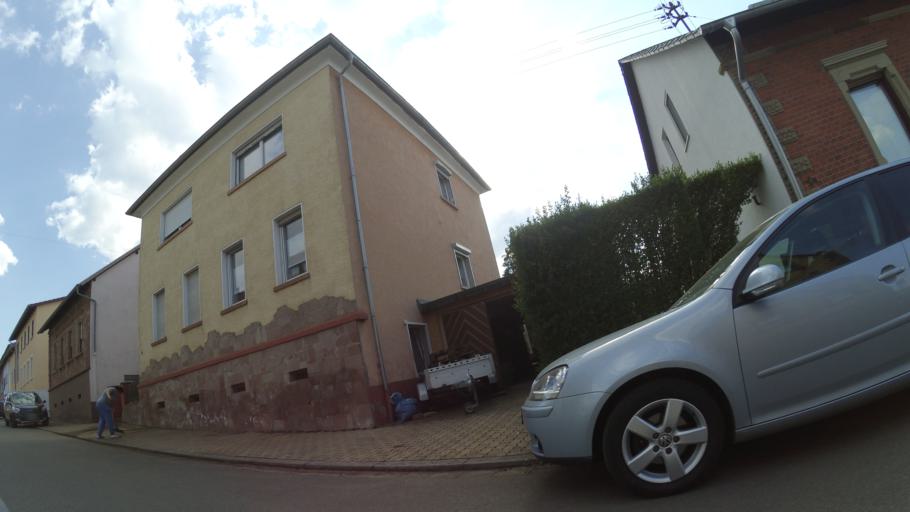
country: DE
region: Saarland
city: Riegelsberg
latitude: 49.3032
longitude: 6.9474
